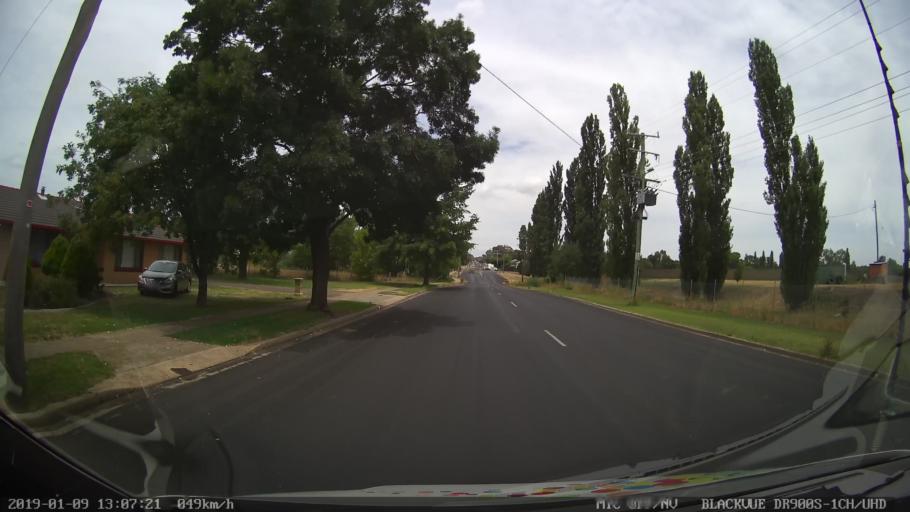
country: AU
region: New South Wales
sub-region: Armidale Dumaresq
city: Armidale
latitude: -30.5190
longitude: 151.6798
